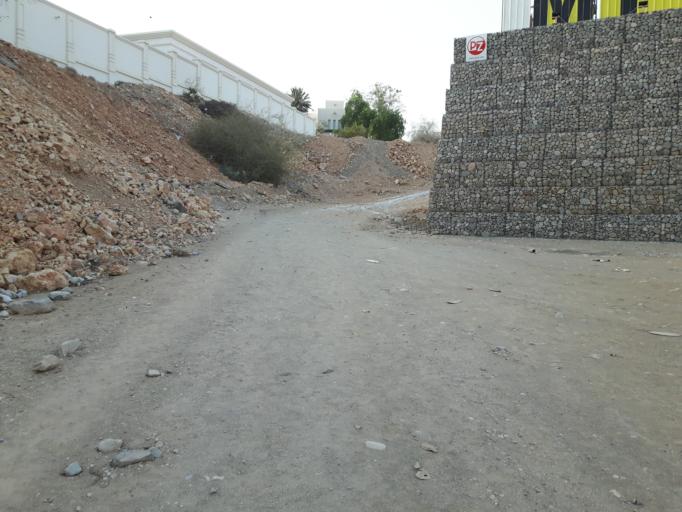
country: OM
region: Muhafazat Masqat
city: Bawshar
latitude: 23.6113
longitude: 58.4723
